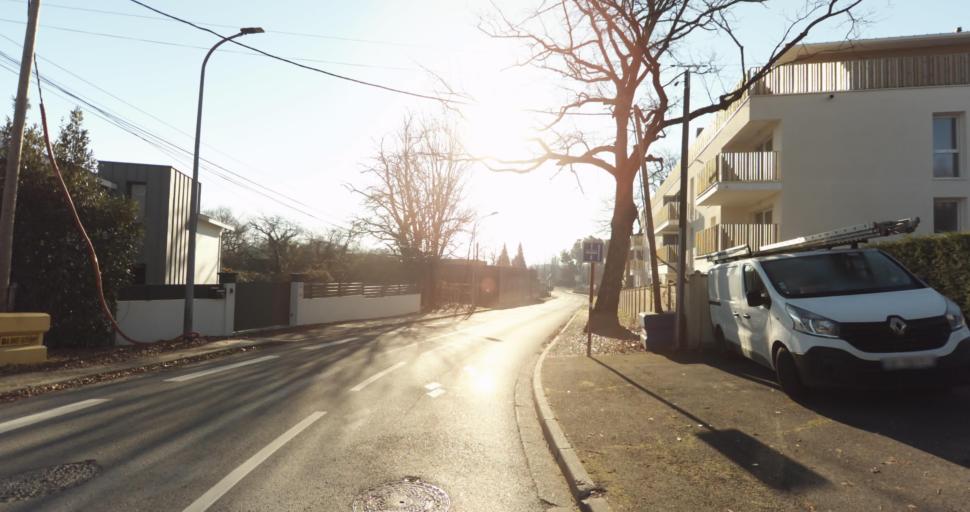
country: FR
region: Aquitaine
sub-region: Departement de la Gironde
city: Carbon-Blanc
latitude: 44.8873
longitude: -0.5097
